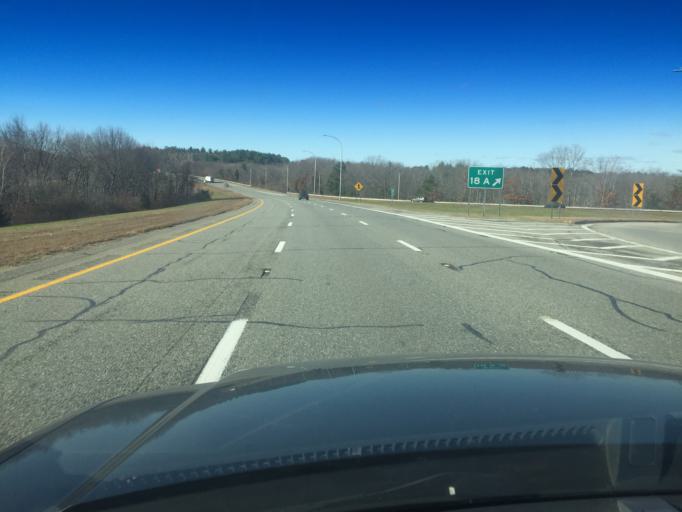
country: US
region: Rhode Island
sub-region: Providence County
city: Cumberland Hill
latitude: 41.9435
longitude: -71.4791
